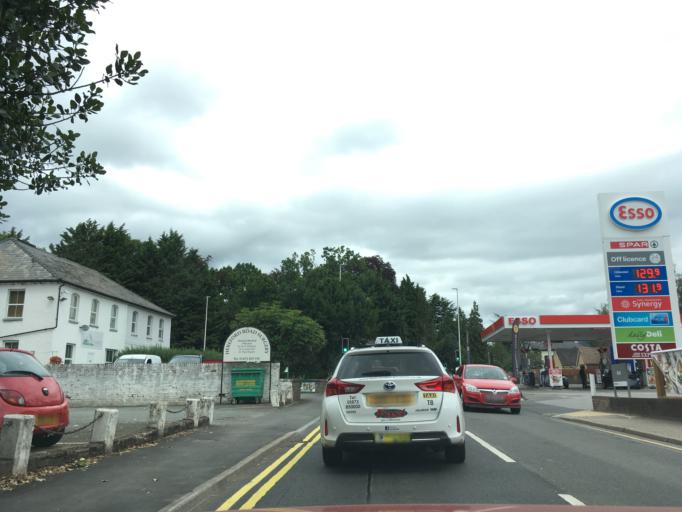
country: GB
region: Wales
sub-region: Monmouthshire
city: Abergavenny
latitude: 51.8234
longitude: -3.0150
